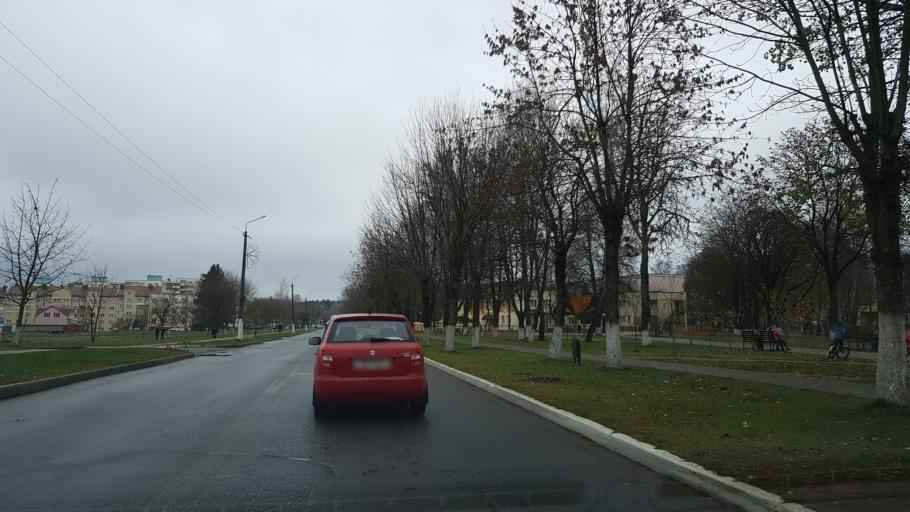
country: BY
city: Fanipol
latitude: 53.7414
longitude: 27.3189
